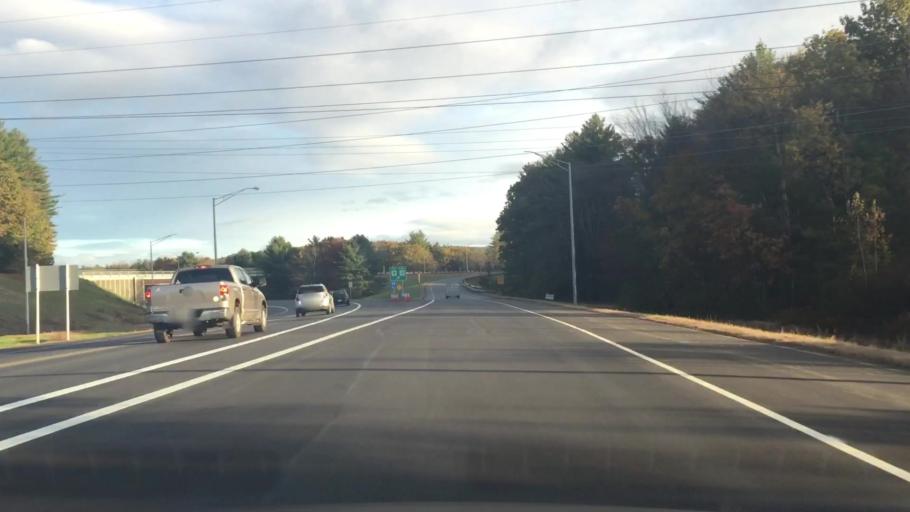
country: US
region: New Hampshire
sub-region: Cheshire County
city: Keene
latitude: 42.9418
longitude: -72.2953
